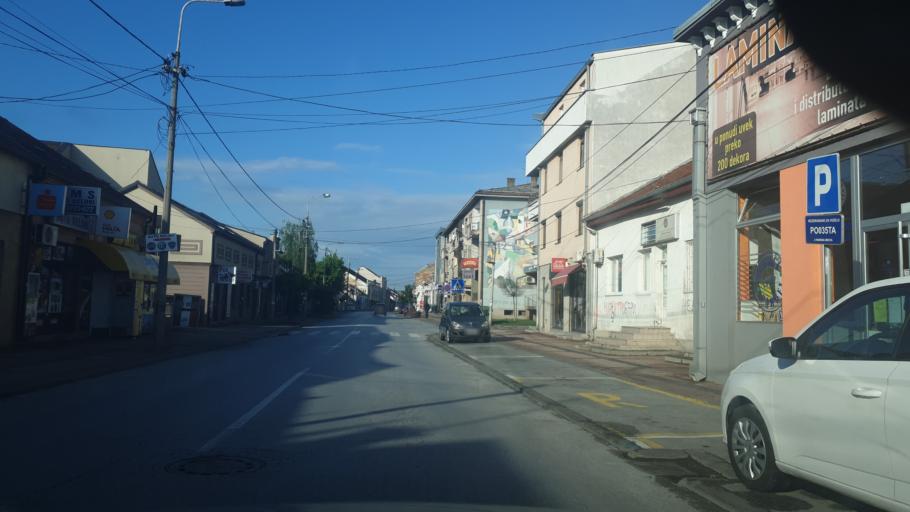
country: RS
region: Central Serbia
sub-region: Belgrade
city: Obrenovac
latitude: 44.6551
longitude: 20.2045
